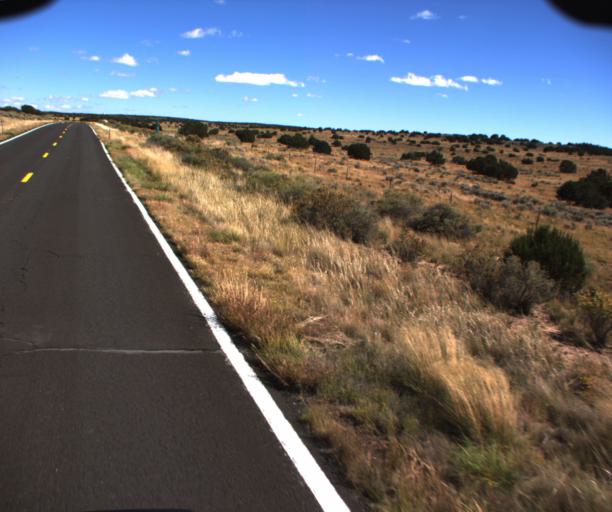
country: US
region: Arizona
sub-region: Apache County
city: Houck
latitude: 34.9335
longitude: -109.1909
